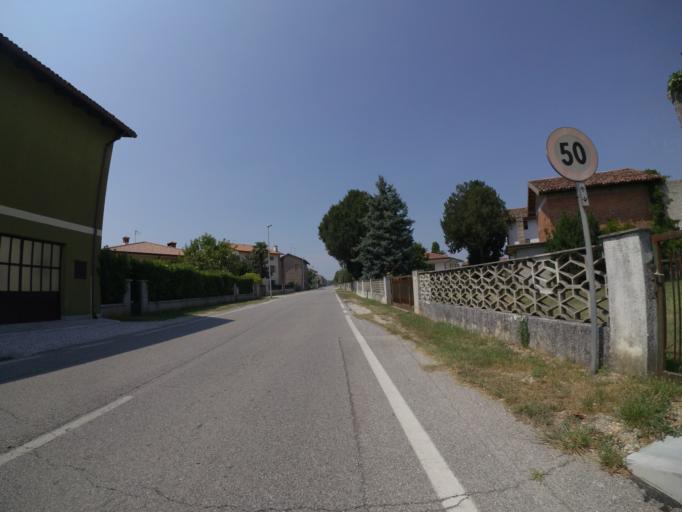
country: IT
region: Friuli Venezia Giulia
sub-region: Provincia di Udine
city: Castions di Strada
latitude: 45.9101
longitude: 13.1789
